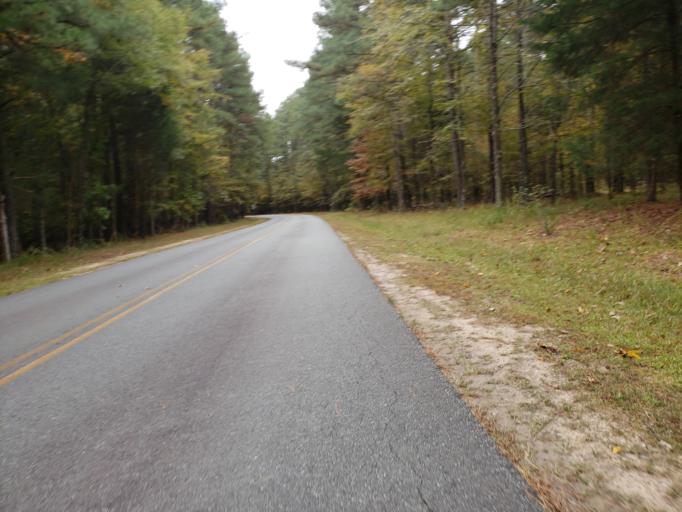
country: US
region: North Carolina
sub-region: Chatham County
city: Fearrington Village
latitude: 35.7508
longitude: -79.0412
